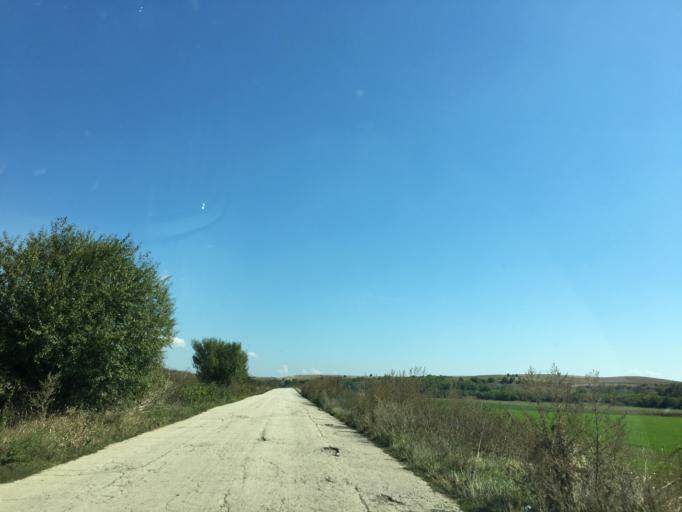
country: BG
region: Pleven
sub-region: Obshtina Knezha
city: Knezha
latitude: 43.5503
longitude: 24.1713
